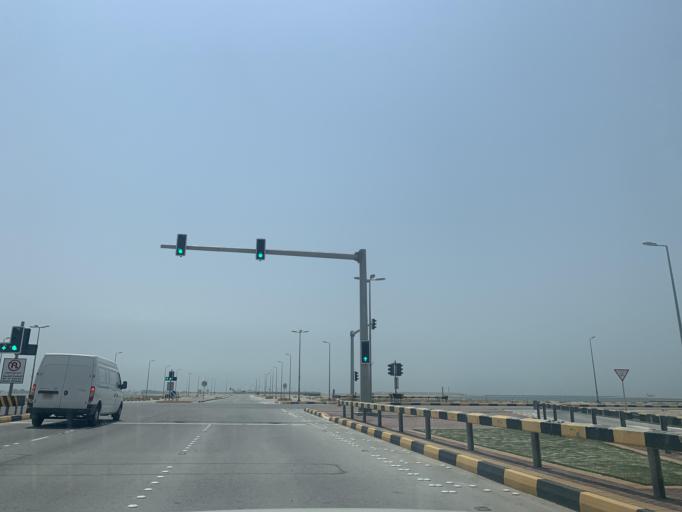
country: BH
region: Central Governorate
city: Dar Kulayb
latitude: 25.8461
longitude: 50.5951
